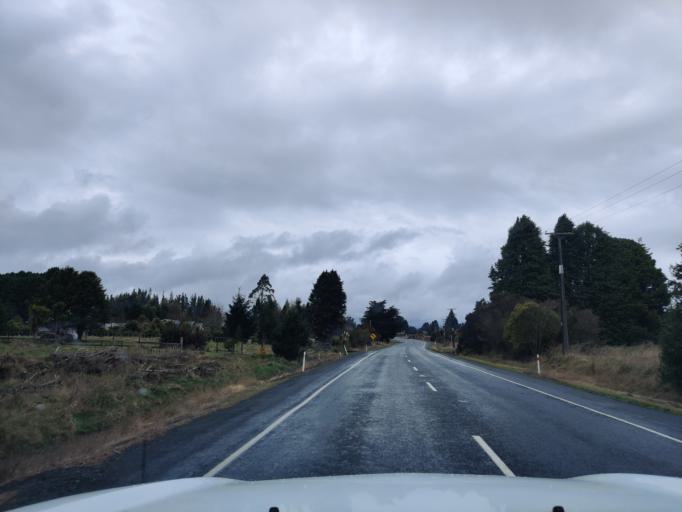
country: NZ
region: Manawatu-Wanganui
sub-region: Ruapehu District
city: Waiouru
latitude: -39.3461
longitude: 175.3726
